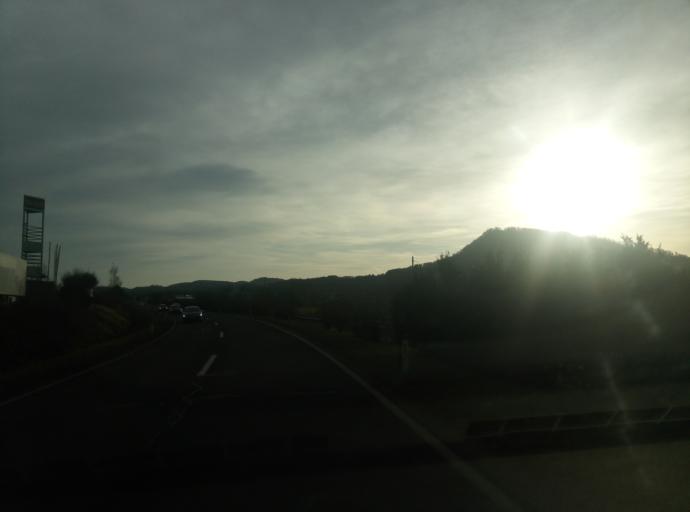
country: SI
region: Sentjur pri Celju
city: Sentjur
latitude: 46.2143
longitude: 15.3844
